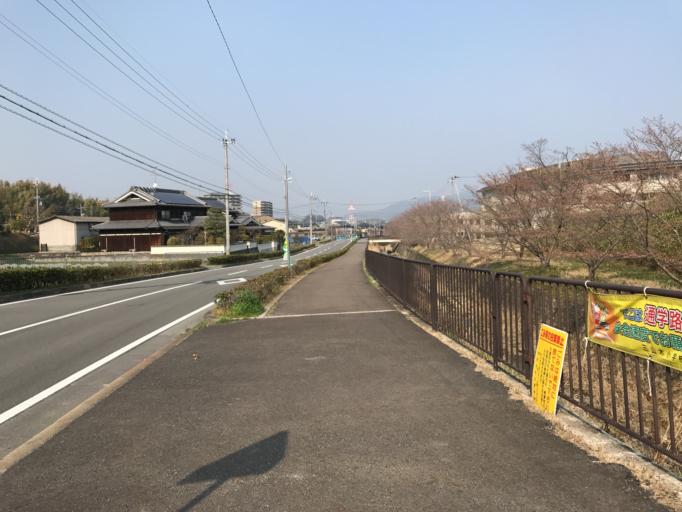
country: JP
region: Kyoto
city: Tanabe
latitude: 34.7930
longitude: 135.7825
